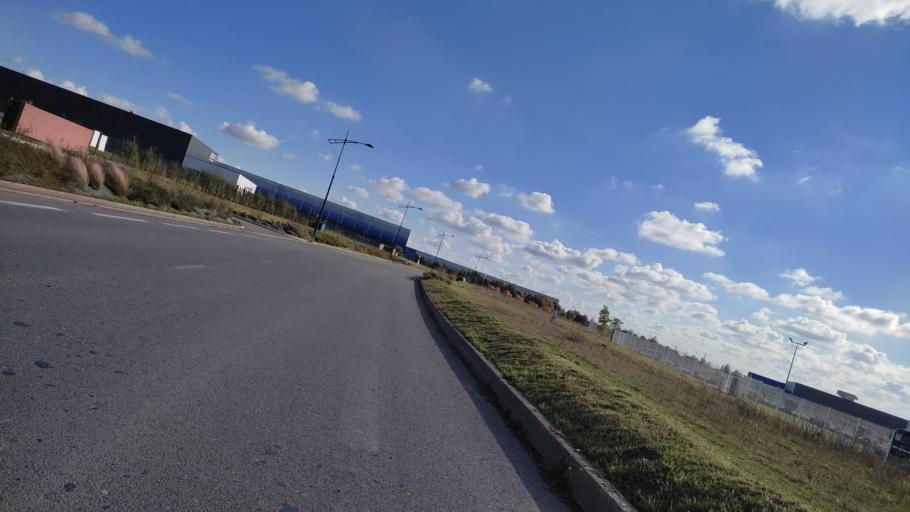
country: FR
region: Nord-Pas-de-Calais
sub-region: Departement du Pas-de-Calais
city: Feuchy
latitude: 50.3178
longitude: 2.8262
